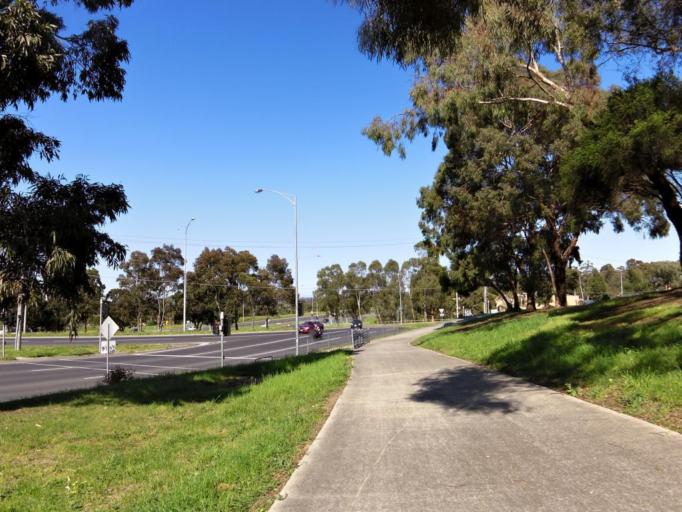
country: AU
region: Victoria
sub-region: Banyule
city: Greensborough
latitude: -37.6883
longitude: 145.1137
